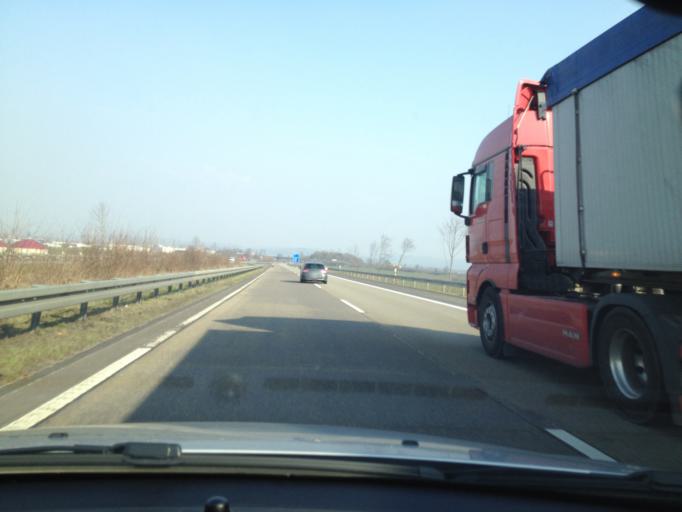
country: DE
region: Hesse
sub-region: Regierungsbezirk Darmstadt
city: Wolfersheim
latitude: 50.4175
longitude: 8.8362
